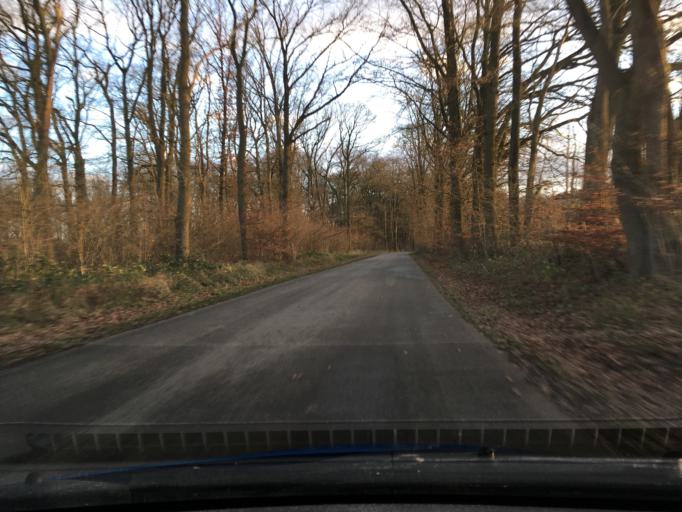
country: DE
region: Lower Saxony
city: Oldendorf
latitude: 53.1408
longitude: 10.2027
